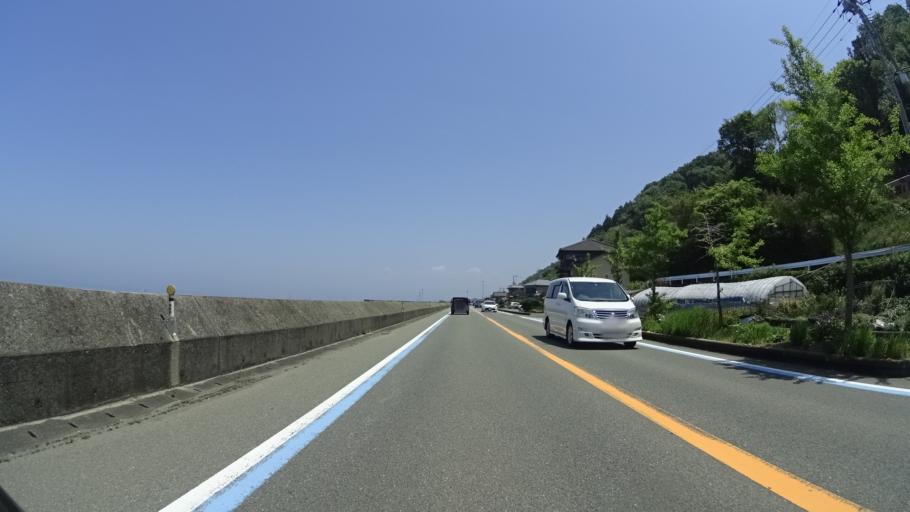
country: JP
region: Ehime
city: Ozu
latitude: 33.6322
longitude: 132.5210
